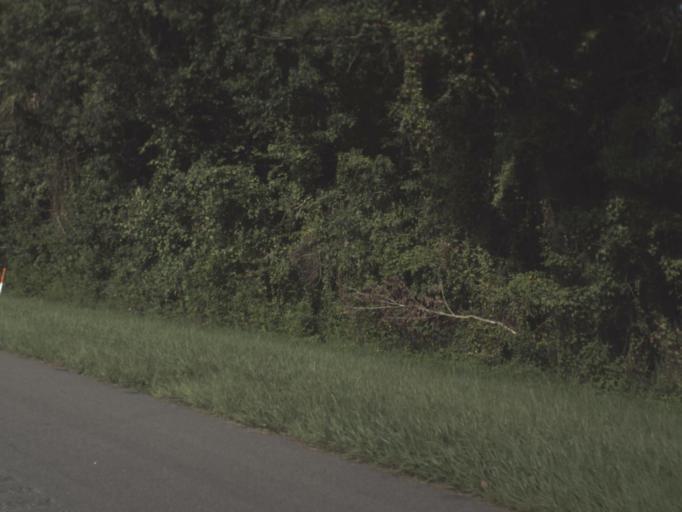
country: US
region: Florida
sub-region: Hillsborough County
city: Lutz
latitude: 28.1439
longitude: -82.4098
